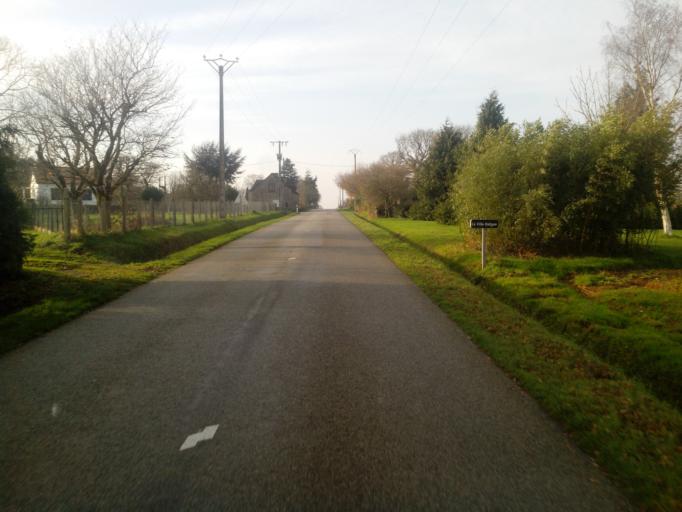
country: FR
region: Brittany
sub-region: Departement du Morbihan
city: Mauron
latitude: 48.0857
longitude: -2.3372
